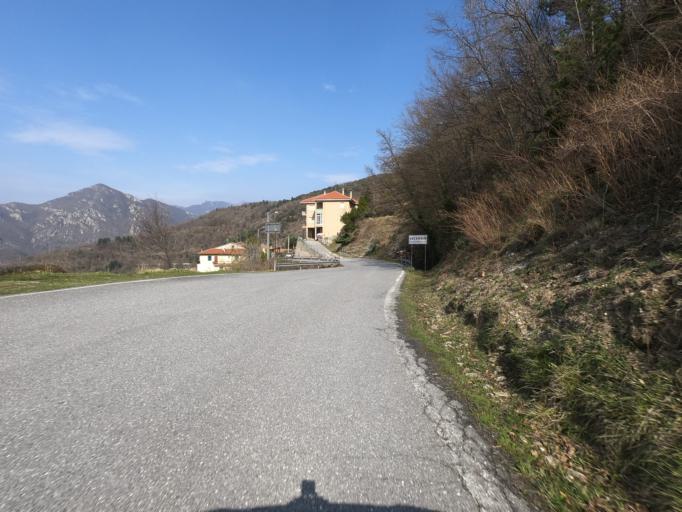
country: IT
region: Liguria
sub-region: Provincia di Savona
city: Castelvecchio di Rocca Barbena
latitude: 44.1251
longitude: 8.1359
